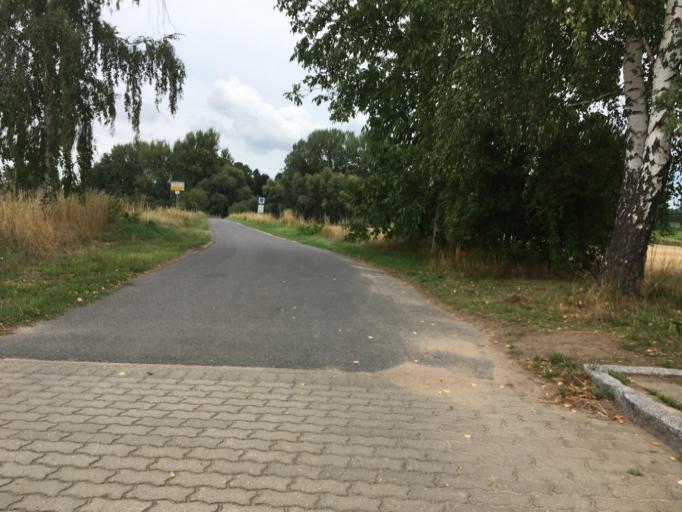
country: DE
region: Brandenburg
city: Prenzlau
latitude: 53.2642
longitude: 13.8492
